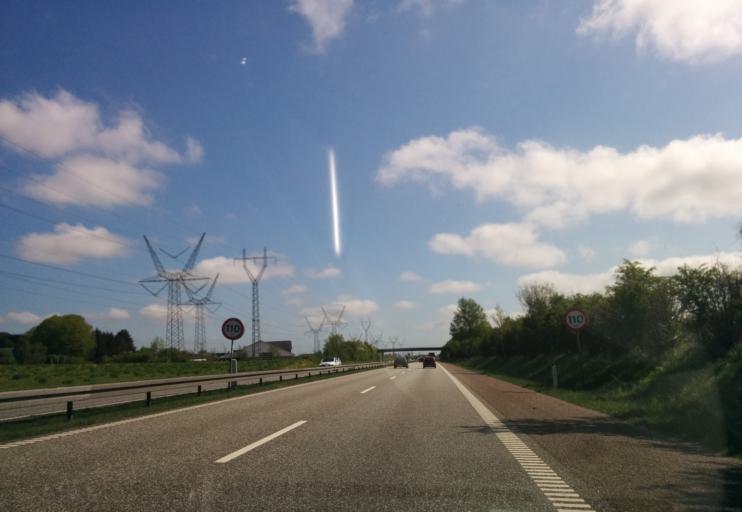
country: DK
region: South Denmark
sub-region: Odense Kommune
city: Neder Holluf
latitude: 55.3582
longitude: 10.4868
